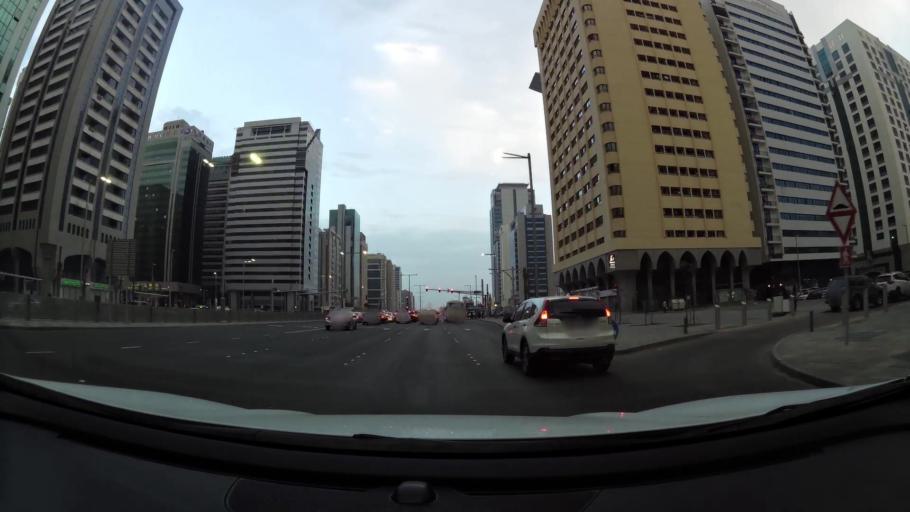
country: AE
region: Abu Dhabi
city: Abu Dhabi
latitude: 24.4951
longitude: 54.3742
